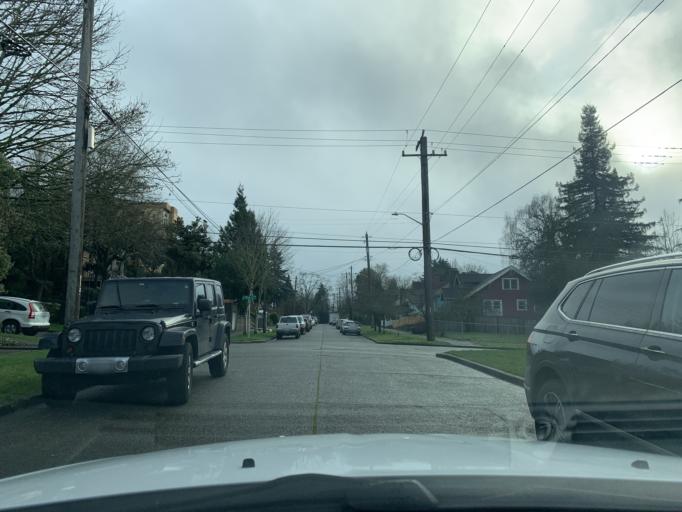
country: US
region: Washington
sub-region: King County
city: Seattle
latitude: 47.6156
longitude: -122.2949
